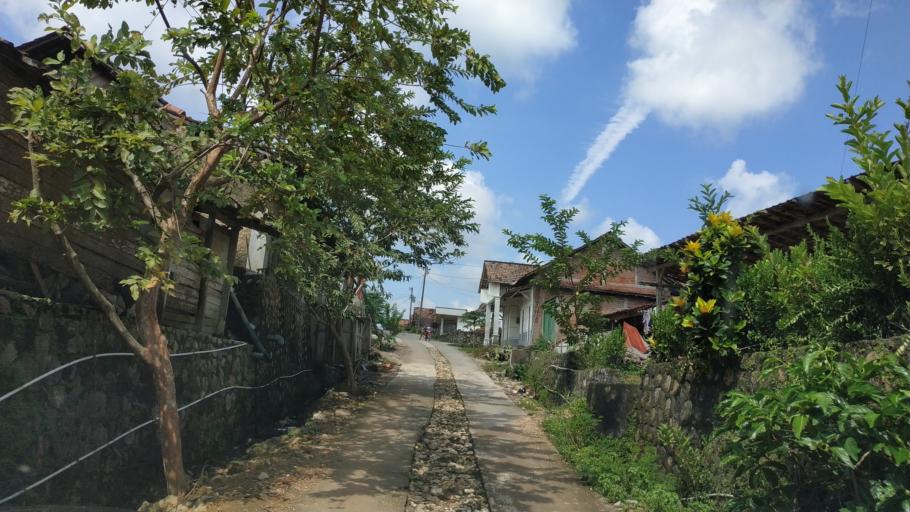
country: ID
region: Central Java
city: Guyangan
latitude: -7.0060
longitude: 111.1064
